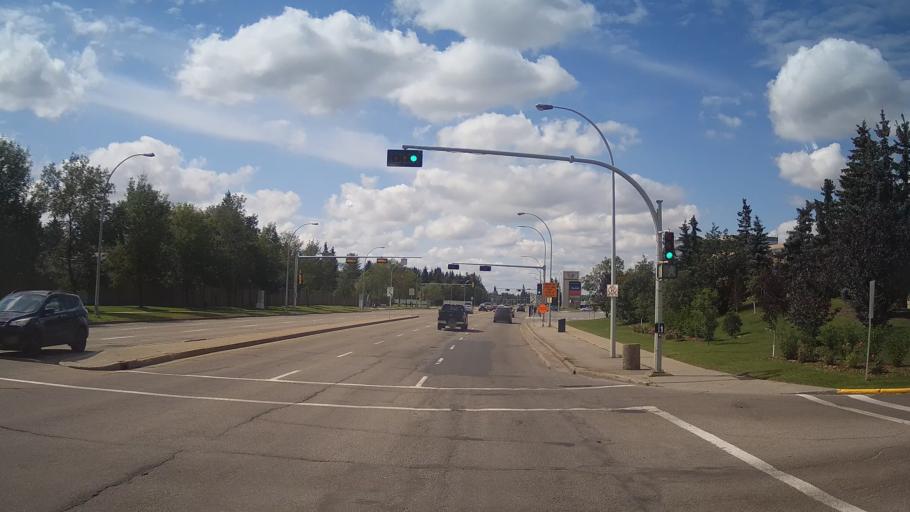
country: CA
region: Alberta
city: St. Albert
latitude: 53.5199
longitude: -113.6204
